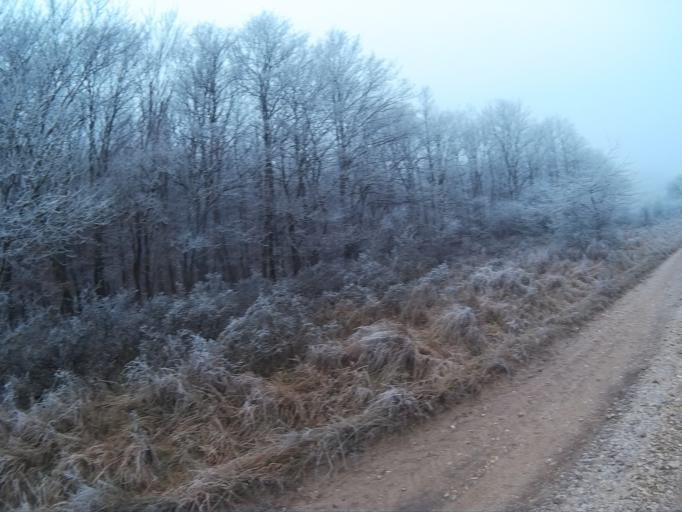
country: HU
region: Fejer
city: Zamoly
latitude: 47.3937
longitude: 18.3611
